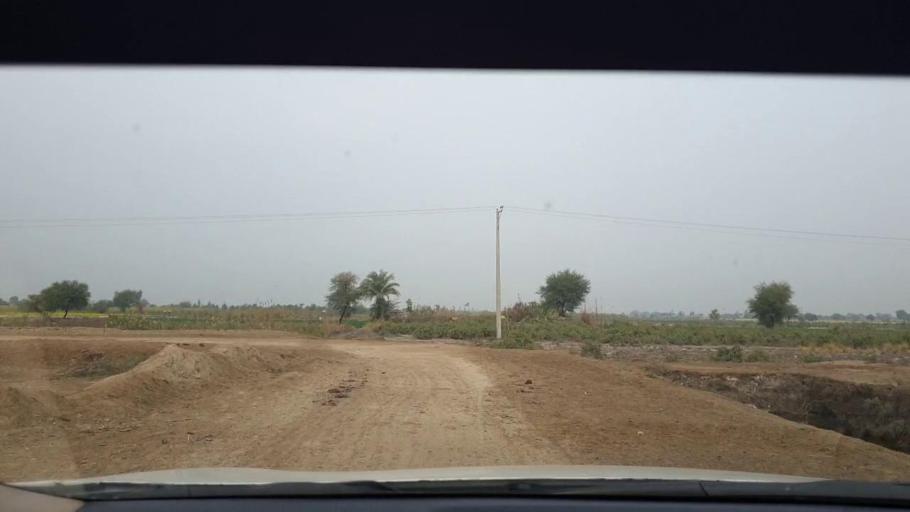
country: PK
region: Sindh
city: Berani
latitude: 25.8291
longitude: 68.8461
